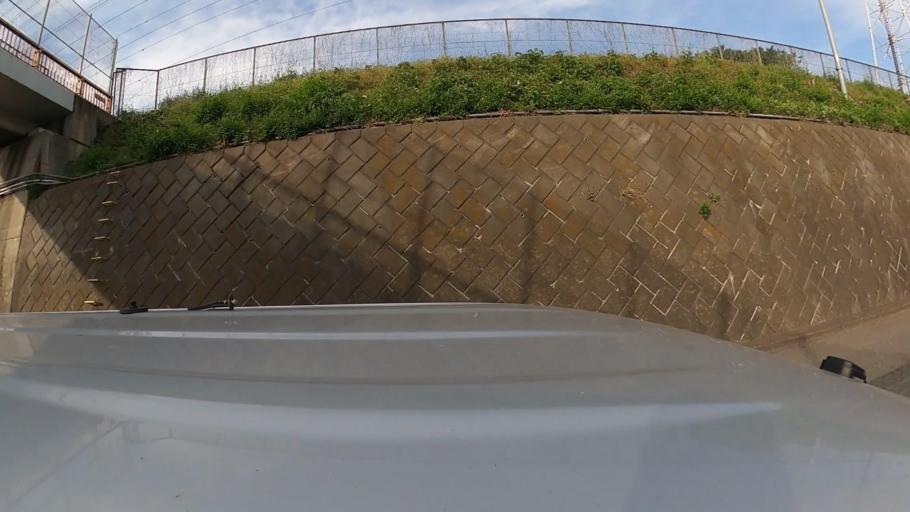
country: JP
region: Saitama
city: Oi
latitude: 35.8324
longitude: 139.5073
